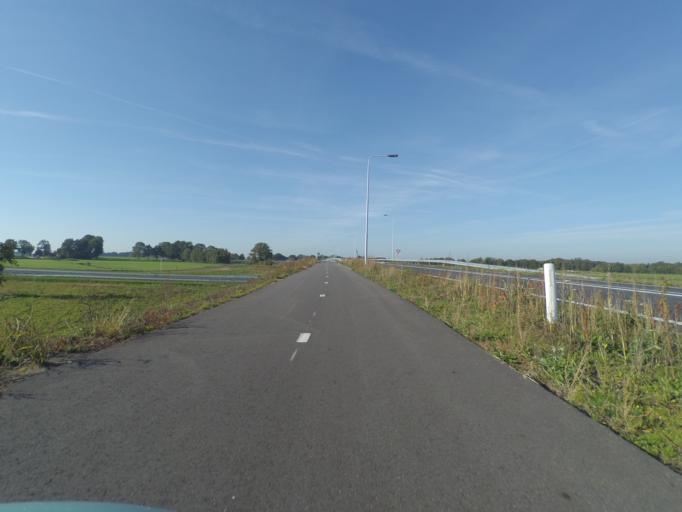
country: NL
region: Gelderland
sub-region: Berkelland
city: Eibergen
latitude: 52.0865
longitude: 6.6334
